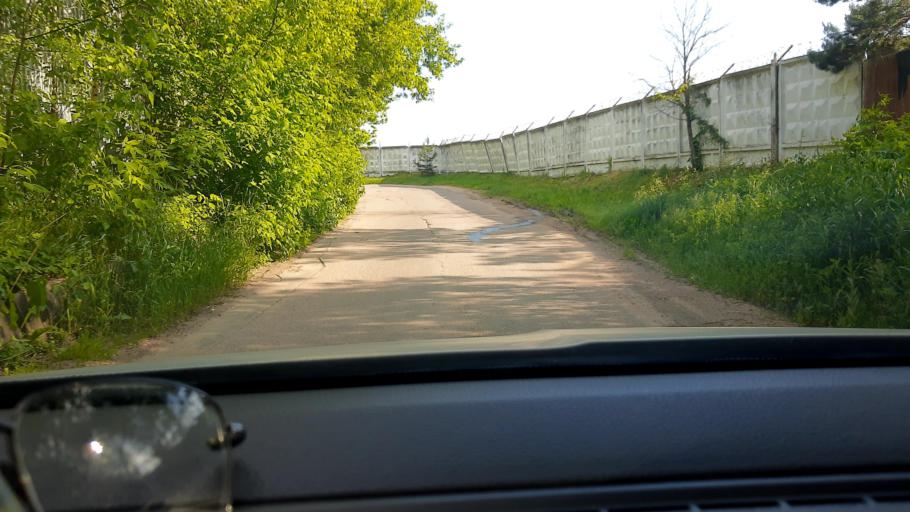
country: RU
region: Moscow
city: Novo-Peredelkino
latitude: 55.6711
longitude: 37.3196
